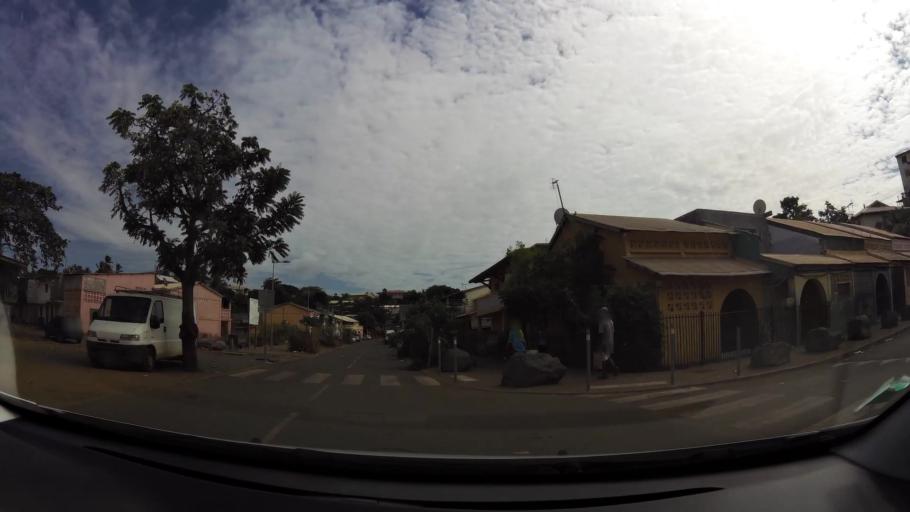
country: YT
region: Mamoudzou
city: Mamoudzou
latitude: -12.7833
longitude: 45.2313
